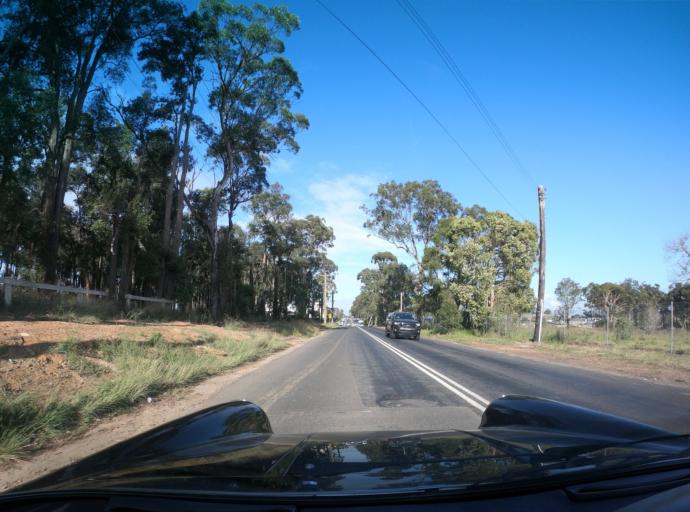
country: AU
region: New South Wales
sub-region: The Hills Shire
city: Beaumont Hills
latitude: -33.6848
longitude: 150.9541
